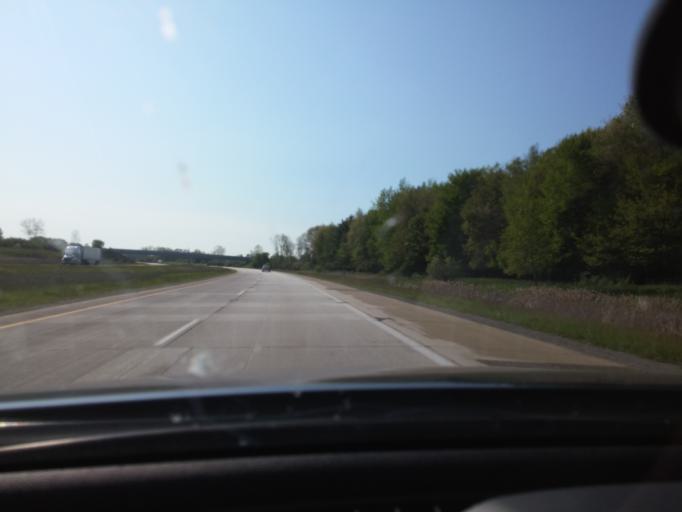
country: US
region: Michigan
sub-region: Lapeer County
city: Lapeer
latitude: 43.0145
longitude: -83.2870
